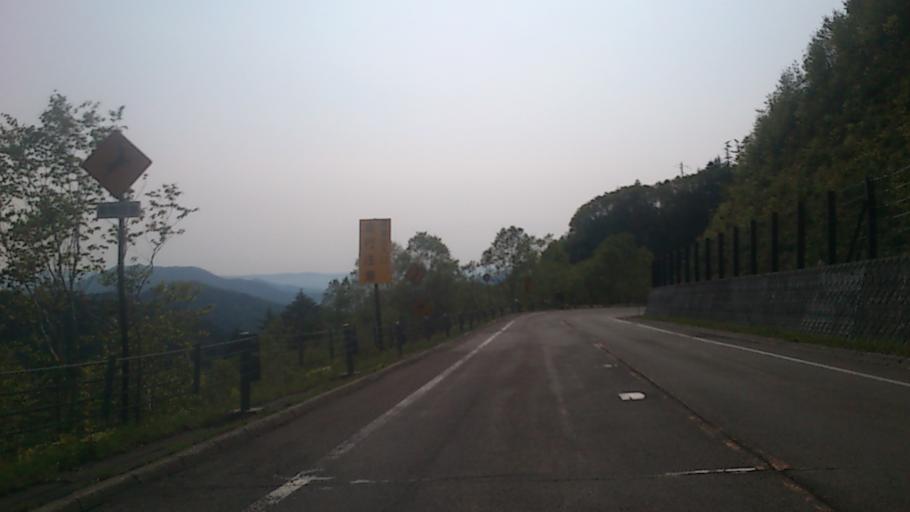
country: JP
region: Hokkaido
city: Bihoro
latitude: 43.4629
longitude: 144.2332
